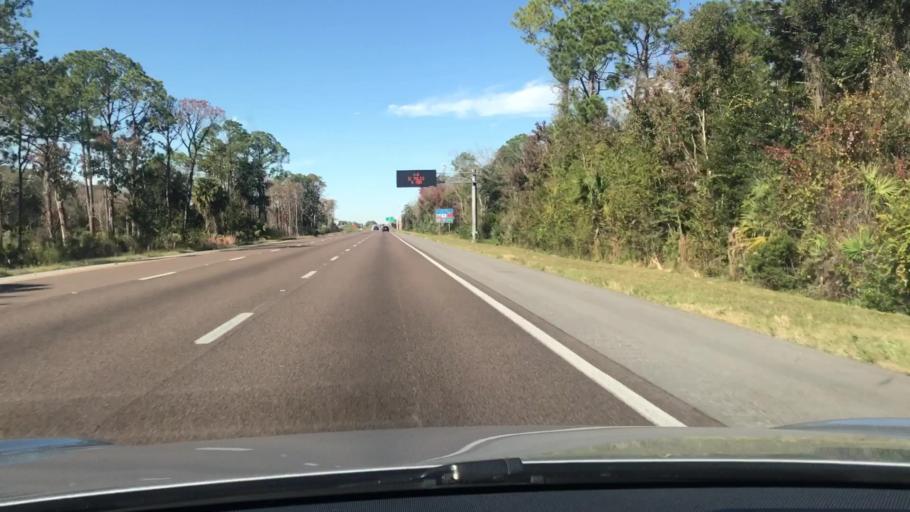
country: US
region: Florida
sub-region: Volusia County
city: Glencoe
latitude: 29.0040
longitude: -80.9818
